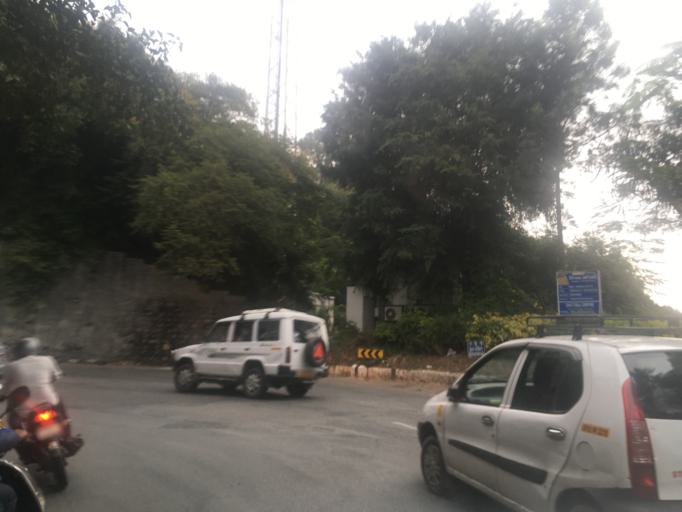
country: IN
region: Andhra Pradesh
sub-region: Chittoor
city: Tirumala
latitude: 13.6672
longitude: 79.3536
